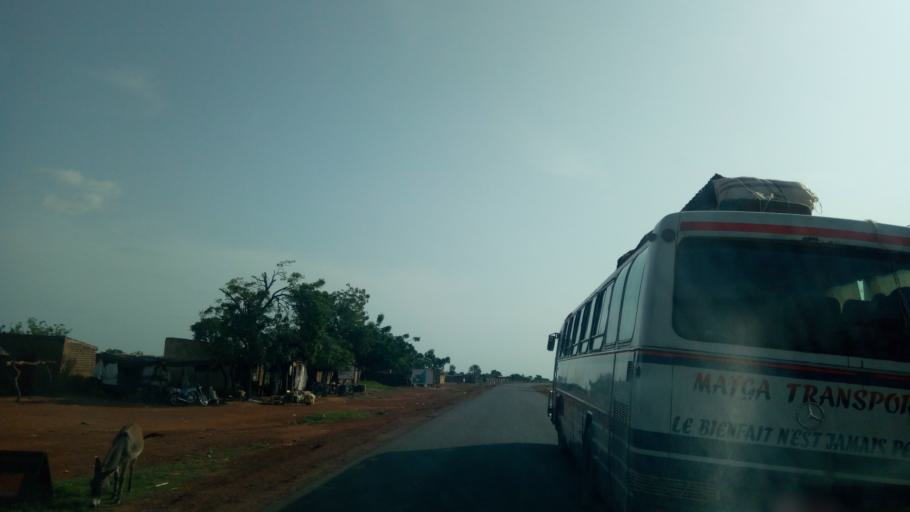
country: ML
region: Sikasso
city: Koutiala
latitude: 12.5223
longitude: -5.2545
